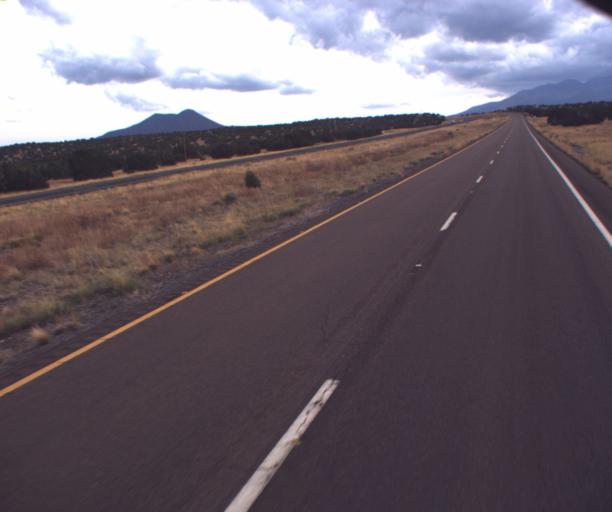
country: US
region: Arizona
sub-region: Coconino County
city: Flagstaff
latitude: 35.4978
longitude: -111.5526
